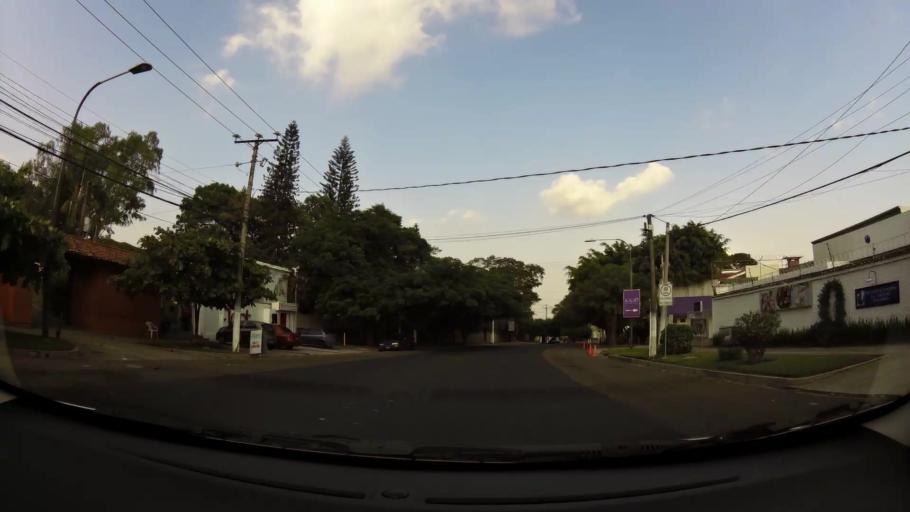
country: SV
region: La Libertad
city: Antiguo Cuscatlan
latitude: 13.6947
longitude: -89.2432
